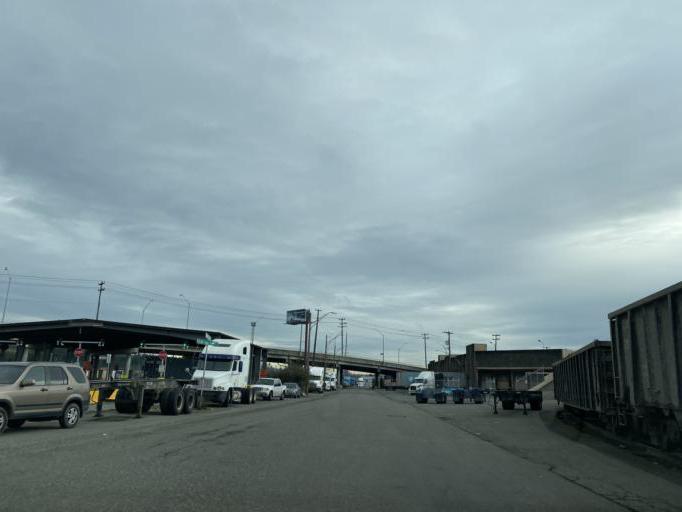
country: US
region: Washington
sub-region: King County
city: Seattle
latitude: 47.5625
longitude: -122.3358
